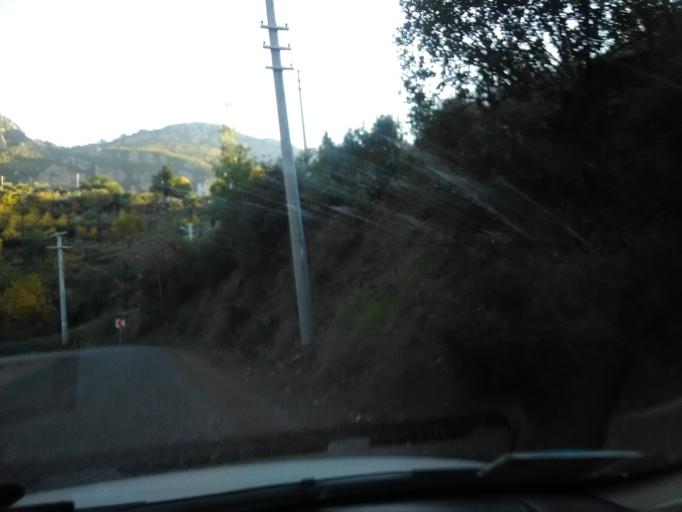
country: TR
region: Antalya
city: Gazipasa
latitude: 36.3106
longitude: 32.4105
